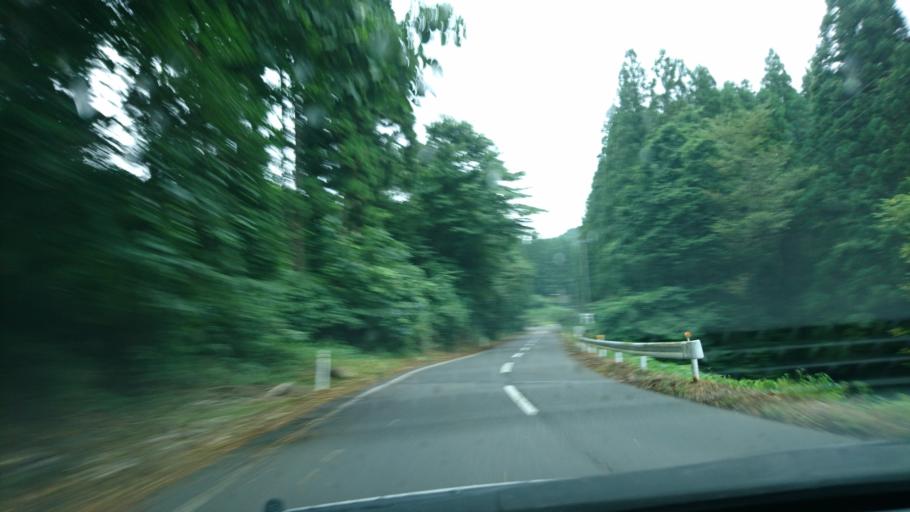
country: JP
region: Iwate
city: Ichinoseki
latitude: 38.8947
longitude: 141.0111
